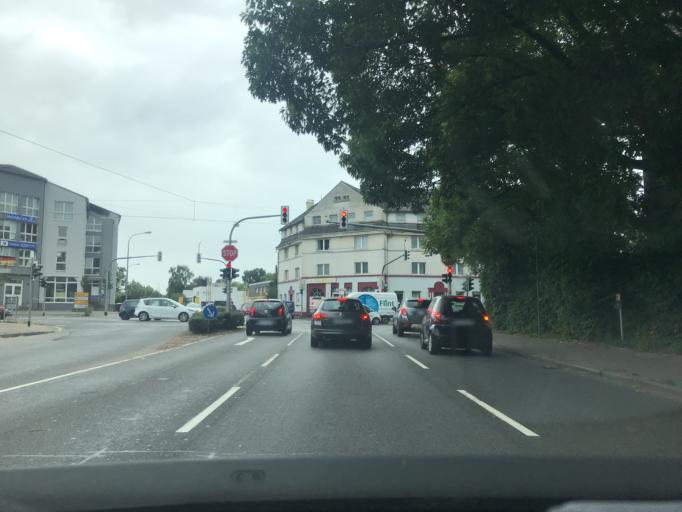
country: DE
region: North Rhine-Westphalia
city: Haan
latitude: 51.1871
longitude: 6.9899
